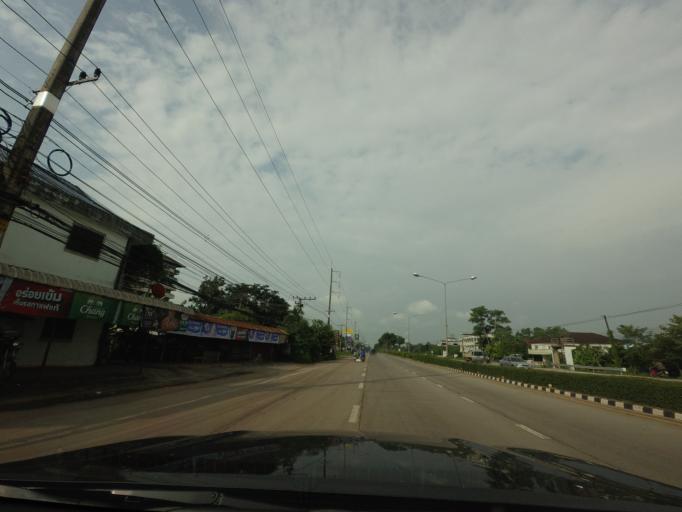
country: TH
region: Nong Khai
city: Nong Khai
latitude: 17.8807
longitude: 102.7521
